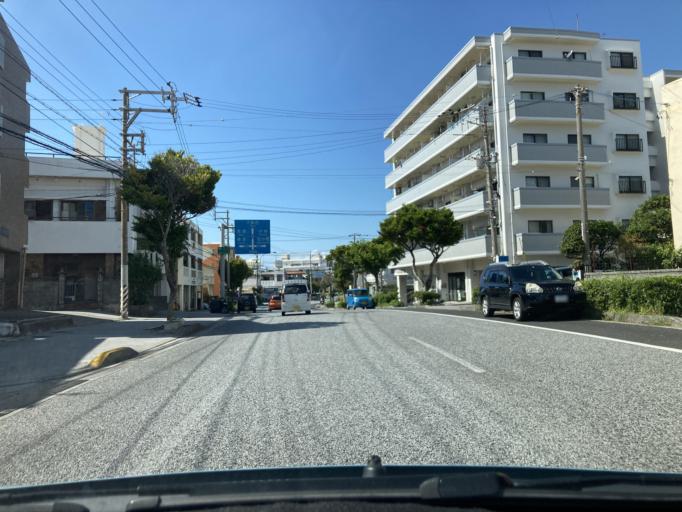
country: JP
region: Okinawa
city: Ginowan
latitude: 26.2544
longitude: 127.7562
